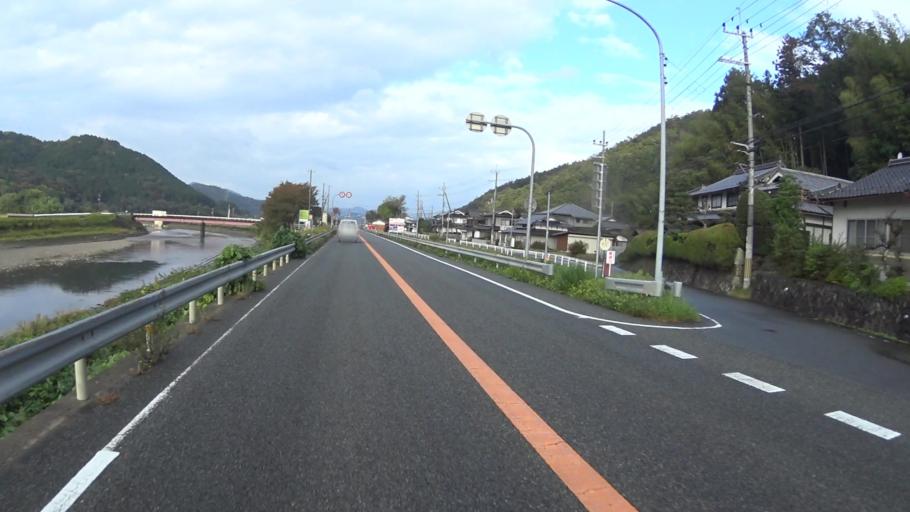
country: JP
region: Kyoto
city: Ayabe
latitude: 35.2584
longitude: 135.1982
